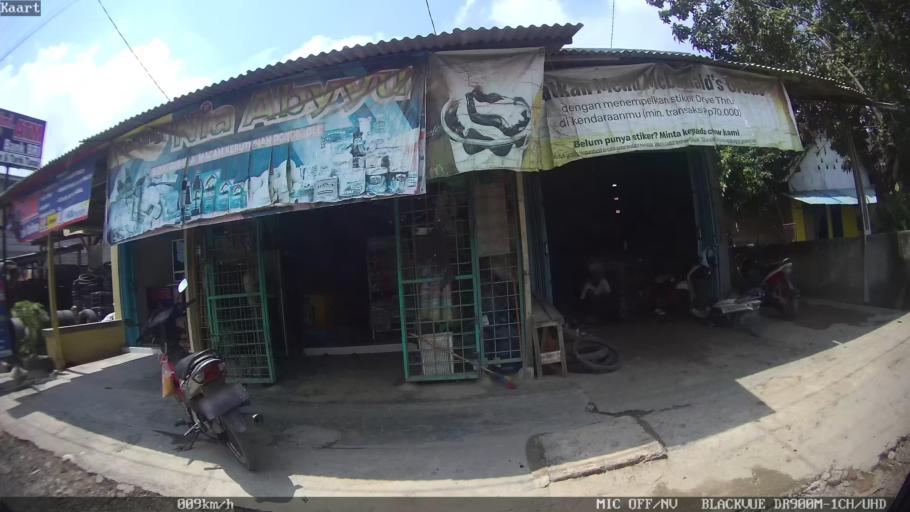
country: ID
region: Lampung
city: Kedaton
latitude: -5.3379
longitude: 105.2952
